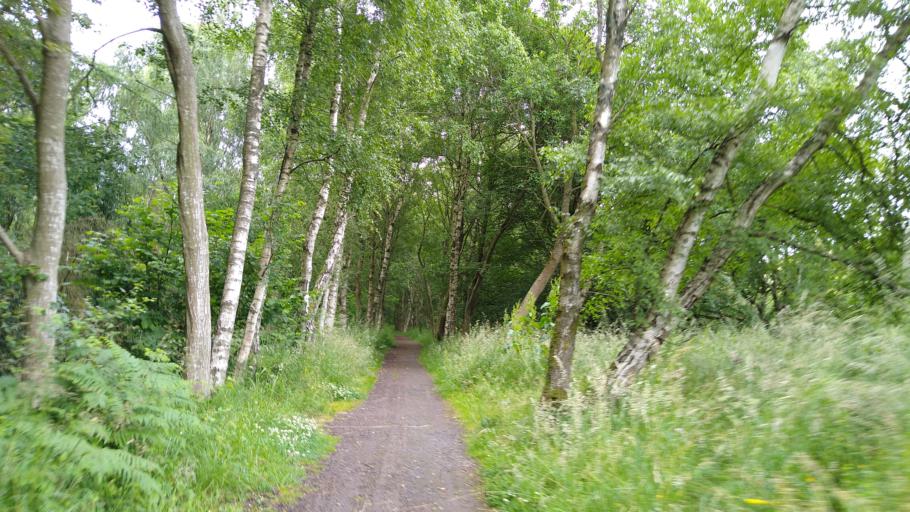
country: GB
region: England
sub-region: Northumberland
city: Greenhead
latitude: 54.9451
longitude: -2.4918
